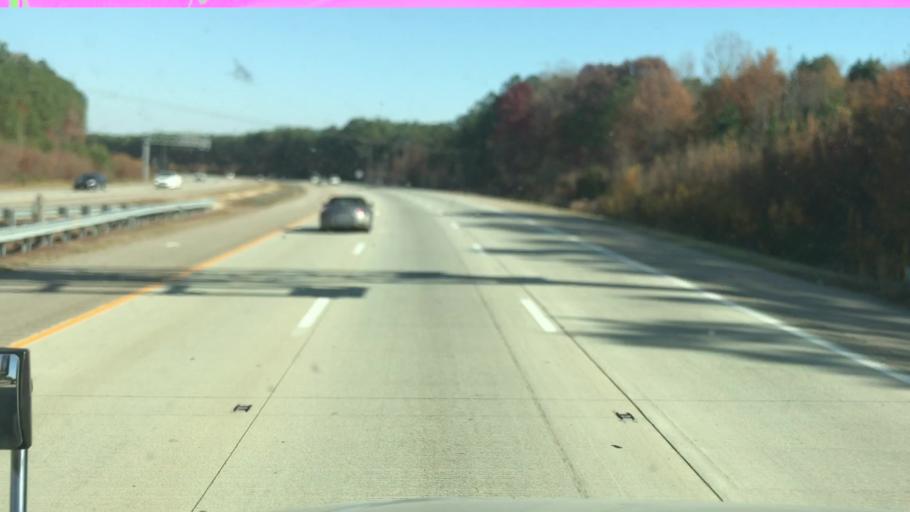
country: US
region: North Carolina
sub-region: Wake County
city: Knightdale
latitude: 35.7700
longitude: -78.4538
